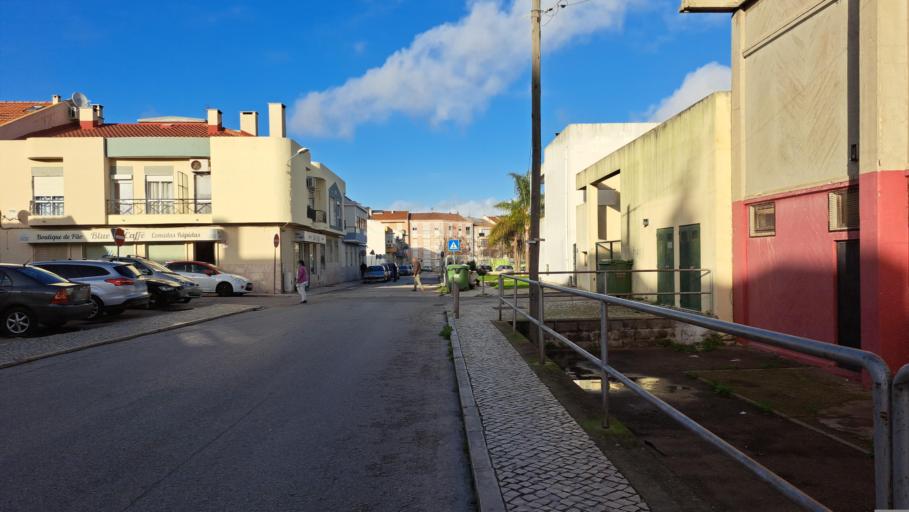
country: PT
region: Setubal
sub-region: Moita
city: Alhos Vedros
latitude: 38.6528
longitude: -9.0444
